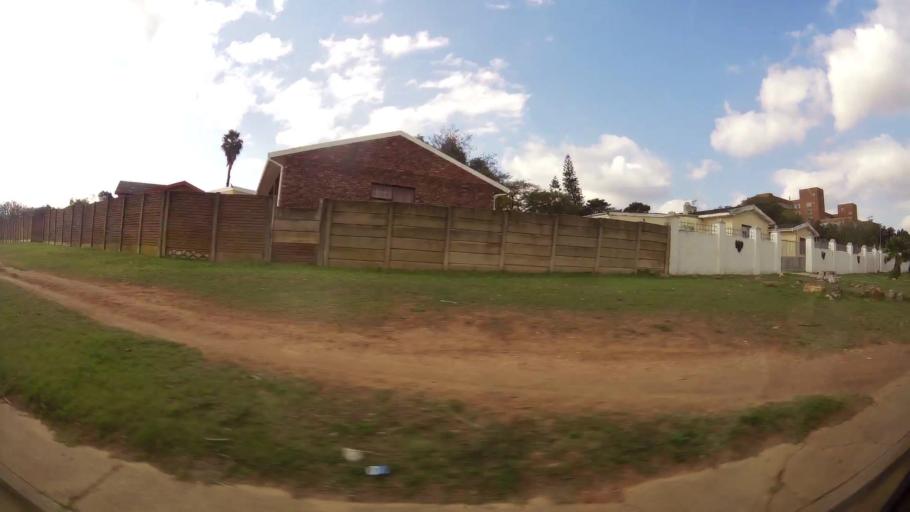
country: ZA
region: Eastern Cape
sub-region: Nelson Mandela Bay Metropolitan Municipality
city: Uitenhage
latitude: -33.7412
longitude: 25.4041
